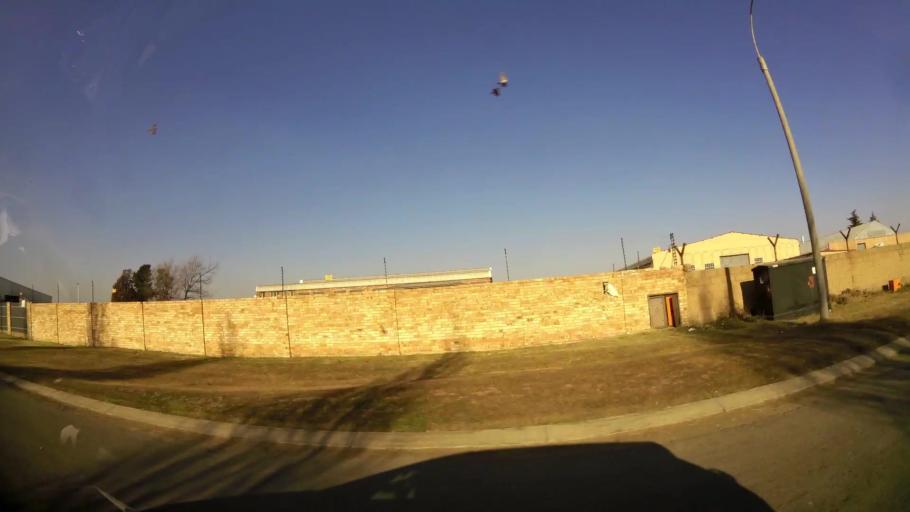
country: ZA
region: Gauteng
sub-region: West Rand District Municipality
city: Randfontein
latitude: -26.1968
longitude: 27.6949
